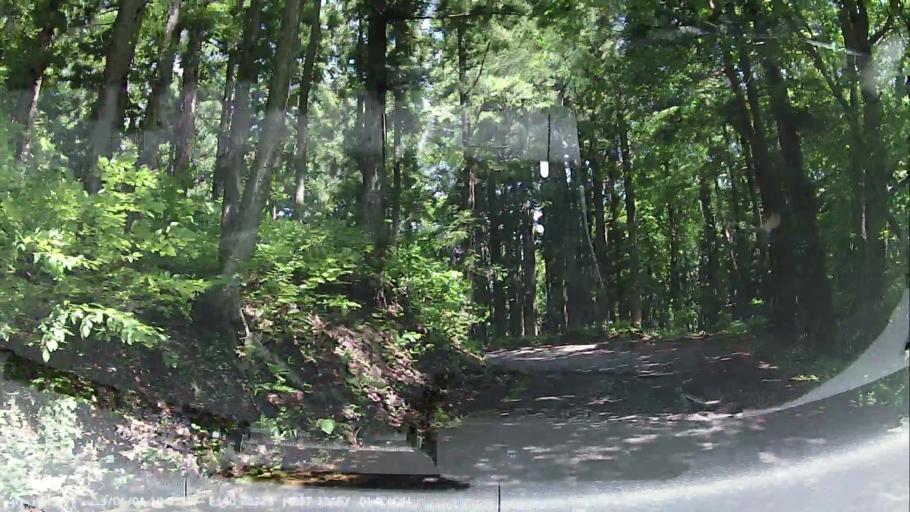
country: JP
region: Fukushima
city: Inawashiro
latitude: 37.3366
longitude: 140.0833
